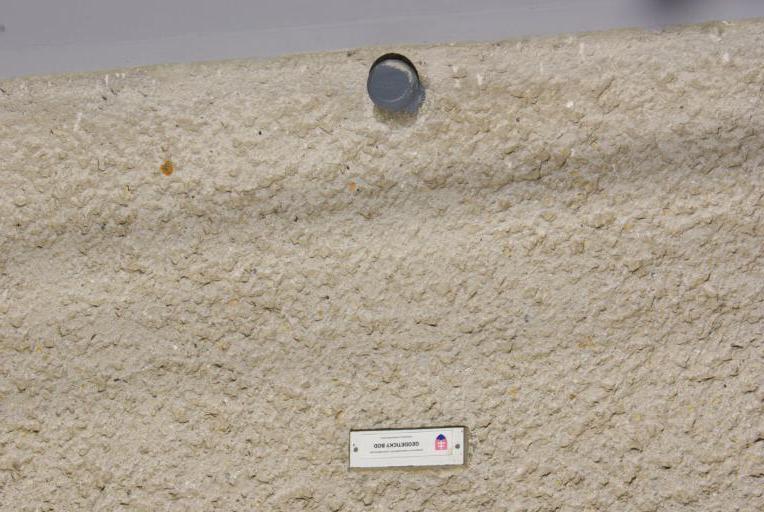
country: SK
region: Banskobystricky
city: Velky Krtis
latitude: 48.2055
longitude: 19.3443
